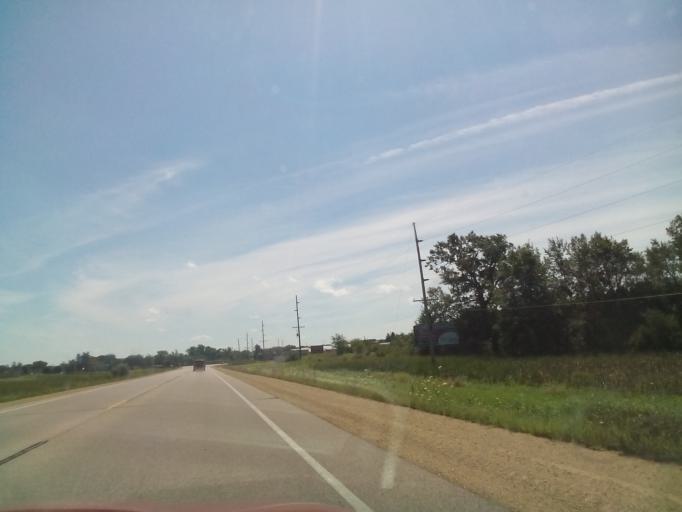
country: US
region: Wisconsin
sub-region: Green County
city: Monticello
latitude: 42.7523
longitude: -89.6053
